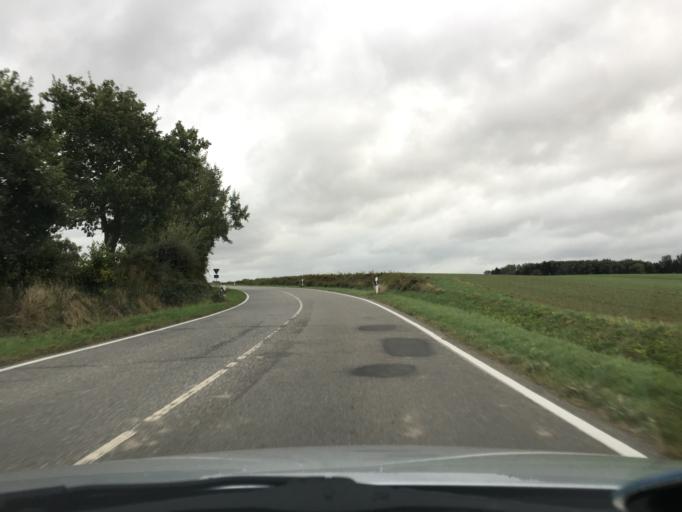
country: DE
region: Schleswig-Holstein
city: Osdorf
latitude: 54.4646
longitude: 10.0443
